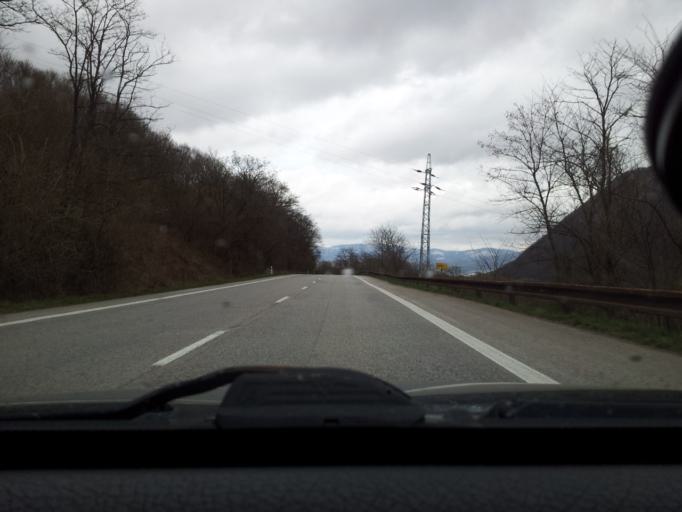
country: SK
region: Kosicky
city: Roznava
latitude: 48.5937
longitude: 20.4713
